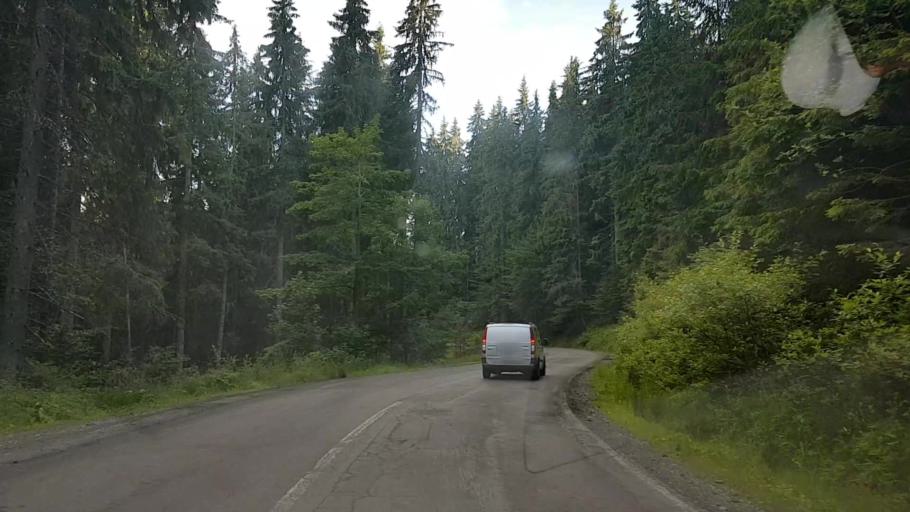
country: RO
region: Harghita
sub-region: Comuna Varsag
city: Varsag
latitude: 46.6661
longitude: 25.3058
